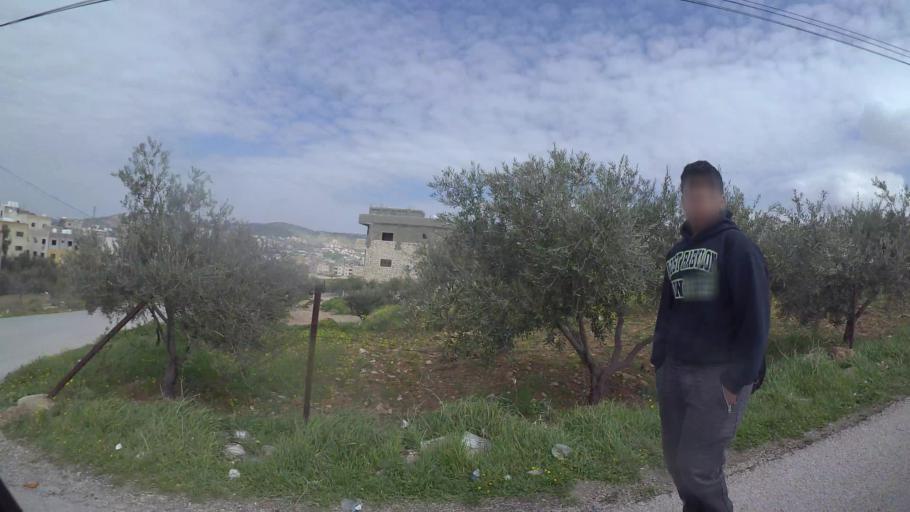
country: JO
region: Amman
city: Al Jubayhah
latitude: 32.0675
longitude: 35.8339
